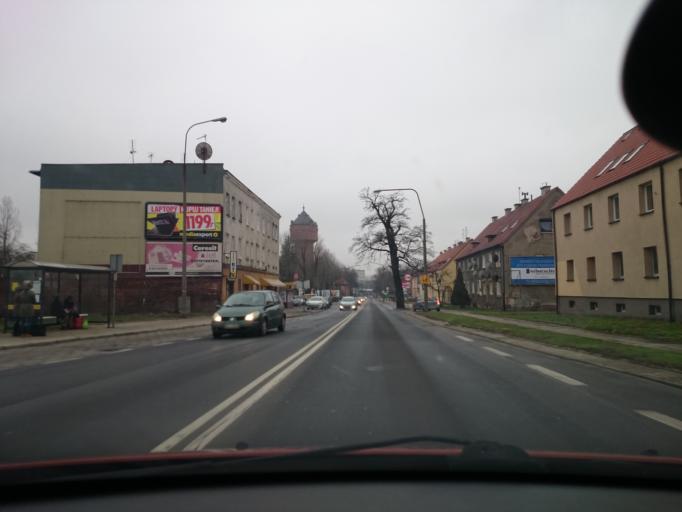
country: PL
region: Opole Voivodeship
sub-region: Powiat opolski
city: Opole
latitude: 50.6779
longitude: 17.9363
